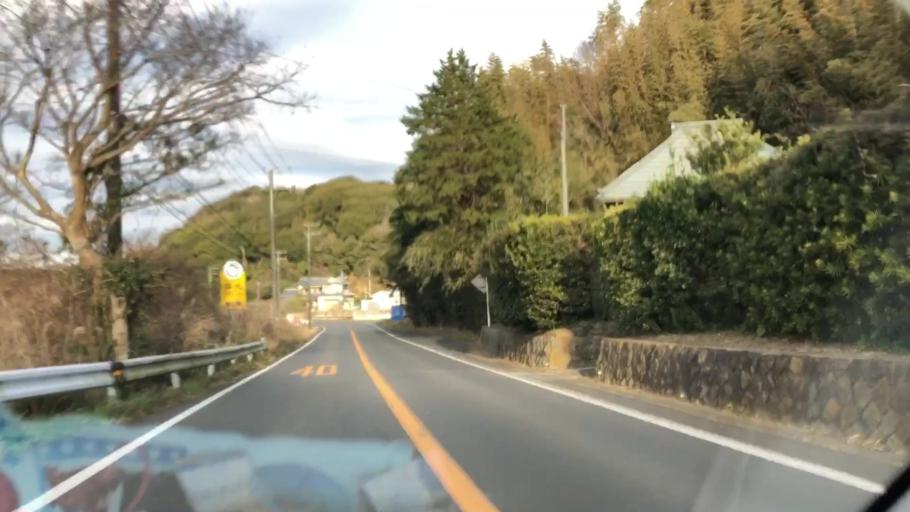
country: JP
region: Chiba
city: Tateyama
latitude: 34.9894
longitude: 139.9277
